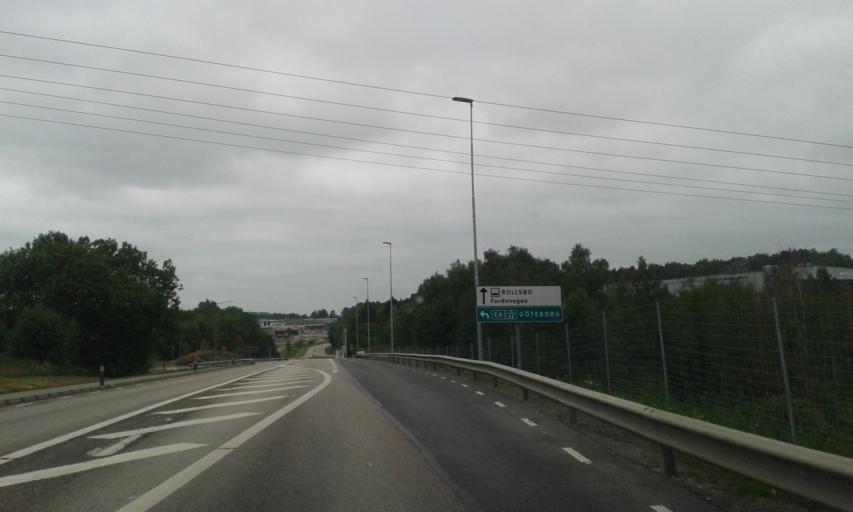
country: SE
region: Vaestra Goetaland
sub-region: Kungalvs Kommun
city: Kungalv
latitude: 57.8840
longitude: 11.9452
